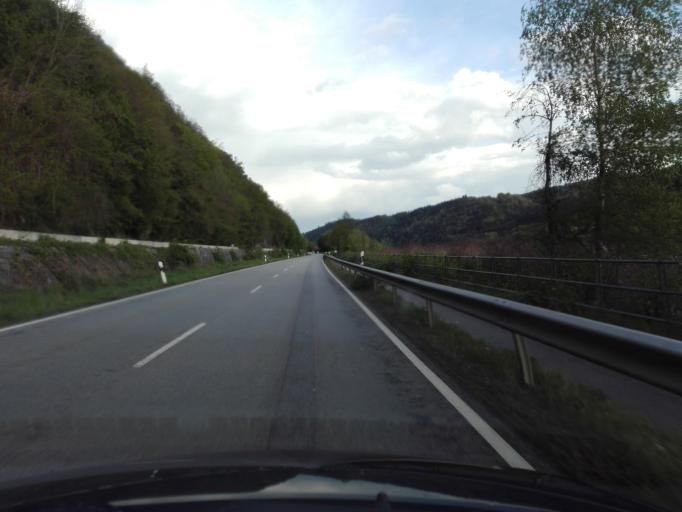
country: DE
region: Bavaria
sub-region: Lower Bavaria
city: Obernzell
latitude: 48.5650
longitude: 13.6102
